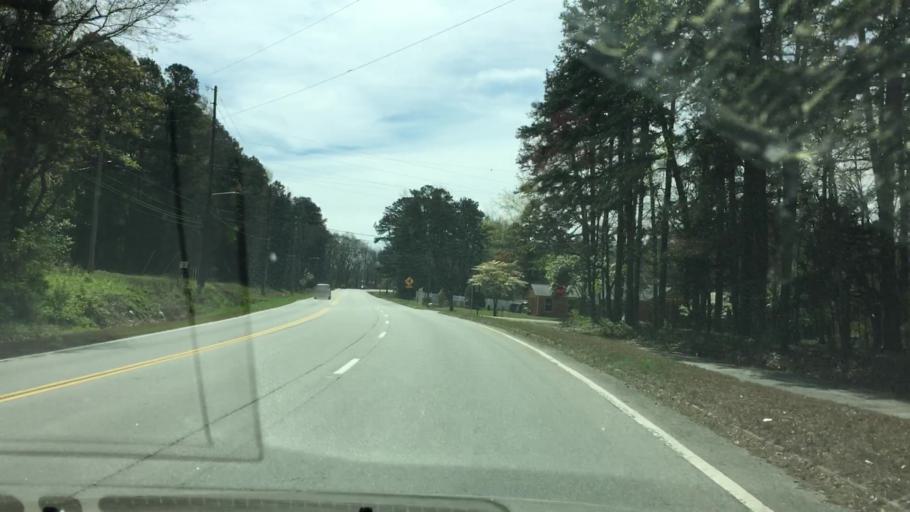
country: US
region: Georgia
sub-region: Barrow County
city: Winder
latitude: 34.0199
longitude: -83.7103
